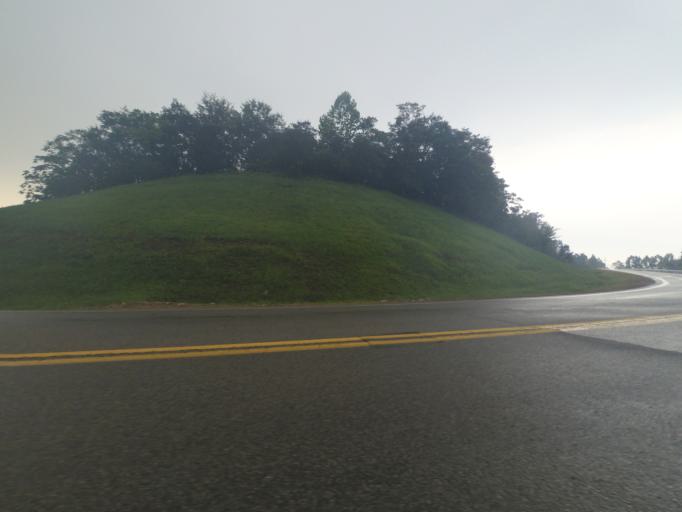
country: US
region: West Virginia
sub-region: Cabell County
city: Huntington
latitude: 38.3886
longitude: -82.3936
